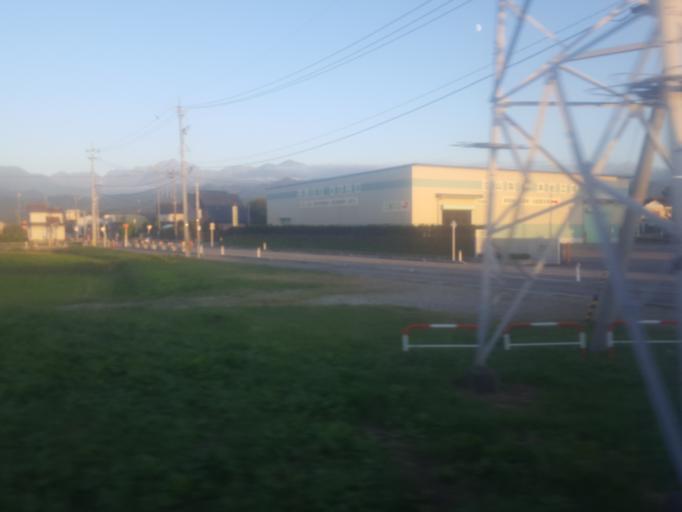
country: JP
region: Toyama
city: Kamiichi
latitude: 36.6698
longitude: 137.3156
